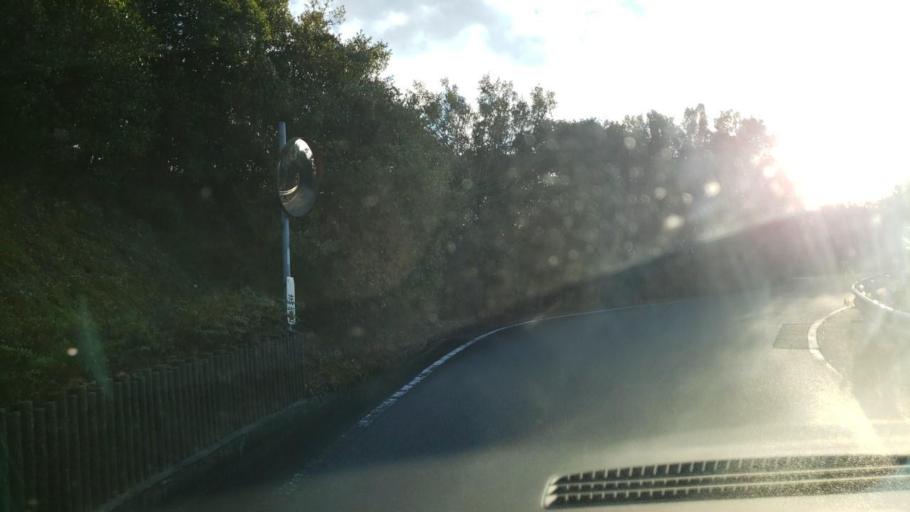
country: JP
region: Hyogo
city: Akashi
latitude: 34.5401
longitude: 134.9629
